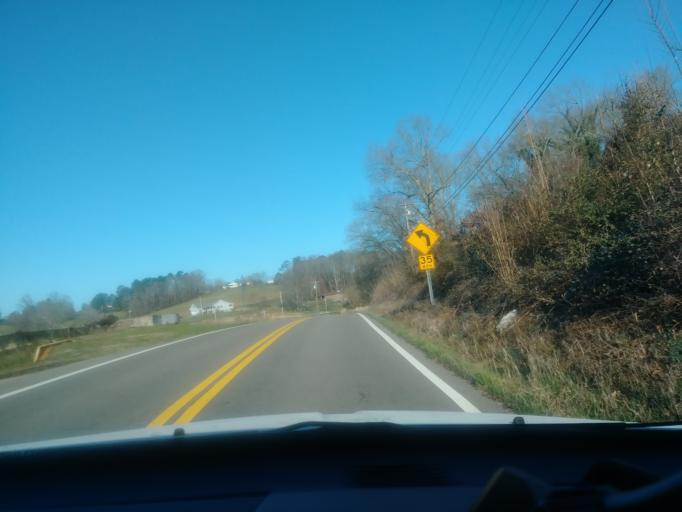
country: US
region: Tennessee
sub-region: Greene County
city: Mosheim
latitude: 36.1137
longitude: -82.9505
